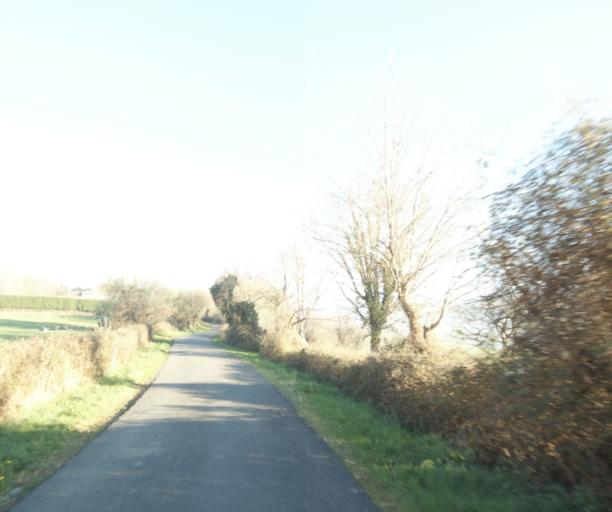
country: FR
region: Aquitaine
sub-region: Departement des Pyrenees-Atlantiques
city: Urrugne
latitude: 43.3480
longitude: -1.7064
